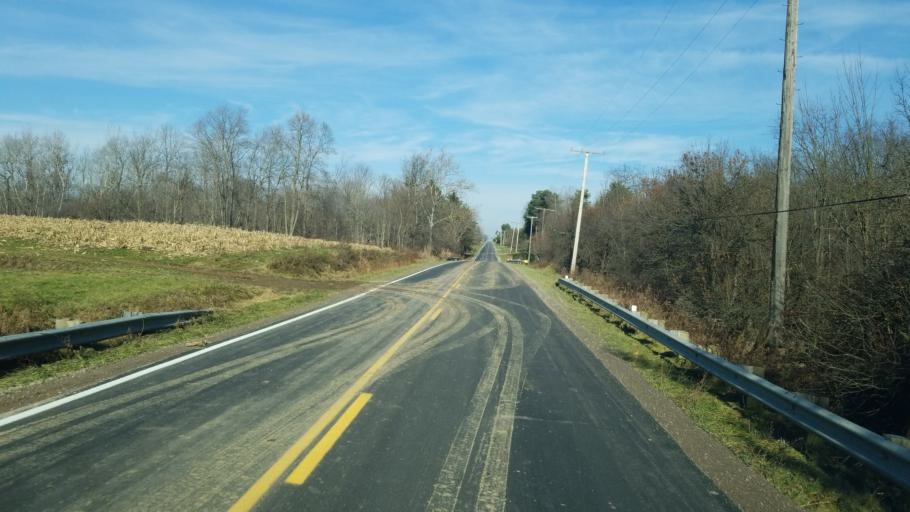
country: US
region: Ohio
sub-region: Ashtabula County
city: Geneva
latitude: 41.7134
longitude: -80.9038
